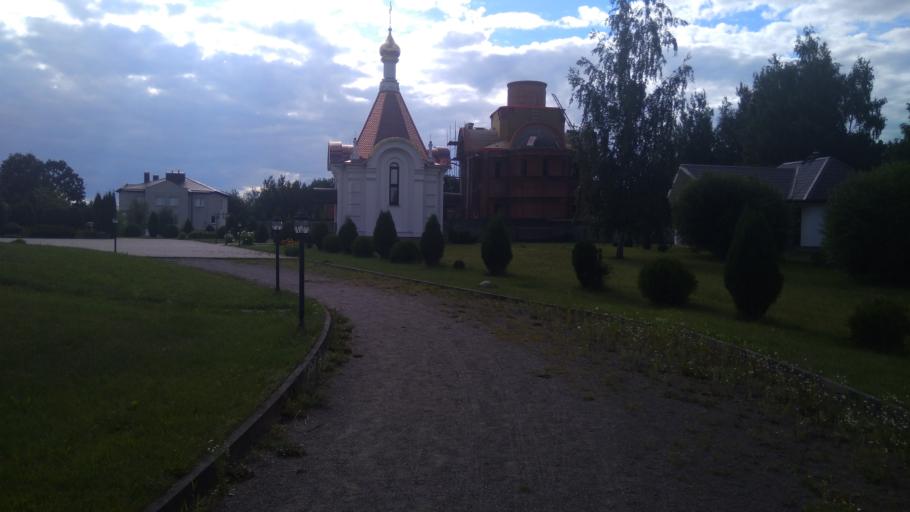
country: BY
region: Minsk
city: Zhdanovichy
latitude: 53.9215
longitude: 27.3888
